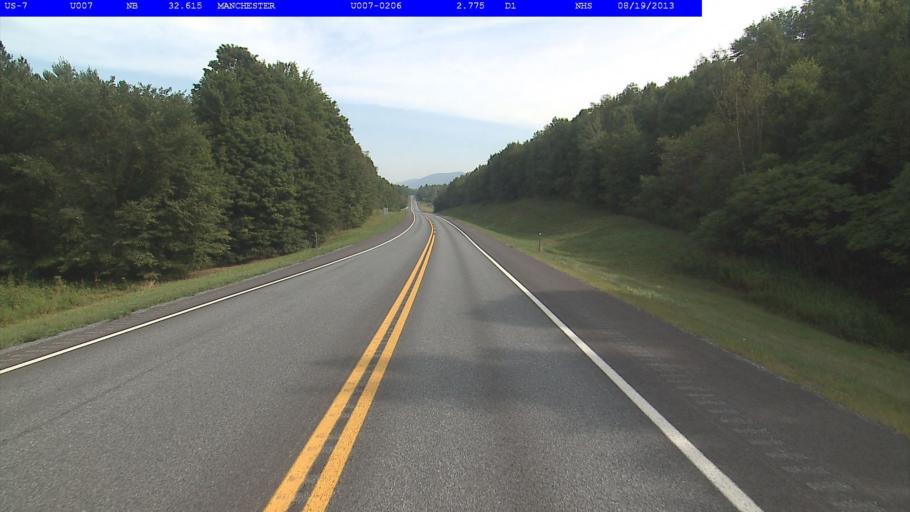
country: US
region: Vermont
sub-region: Bennington County
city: Manchester Center
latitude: 43.1497
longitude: -73.0476
